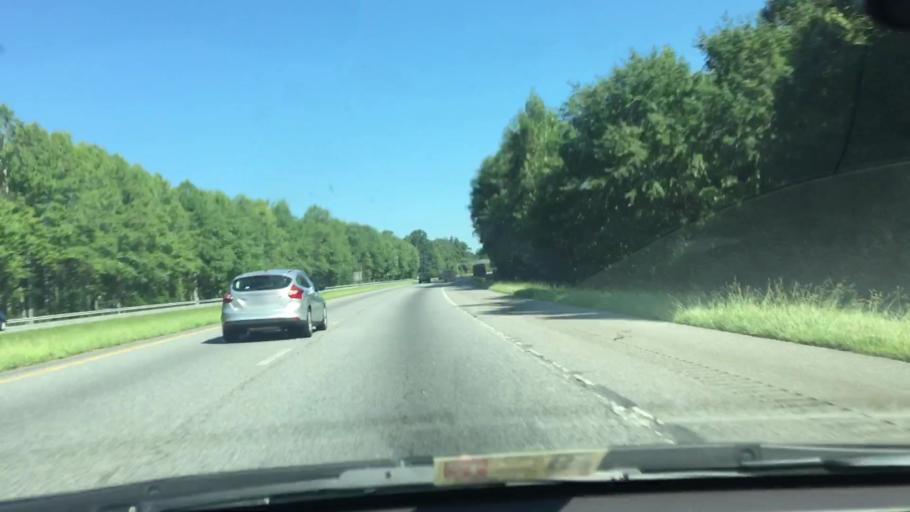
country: US
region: North Carolina
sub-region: Iredell County
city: Statesville
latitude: 35.8596
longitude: -80.8634
